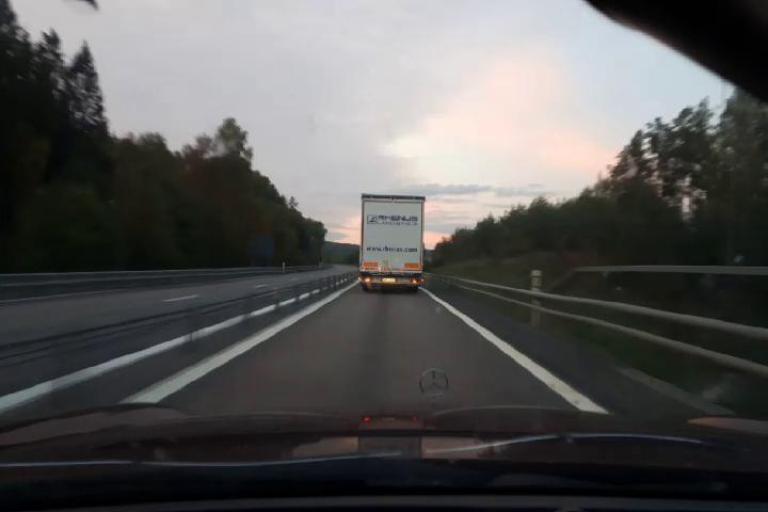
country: SE
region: Vaesternorrland
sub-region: Haernoesands Kommun
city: Haernoesand
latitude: 62.8236
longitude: 17.9701
